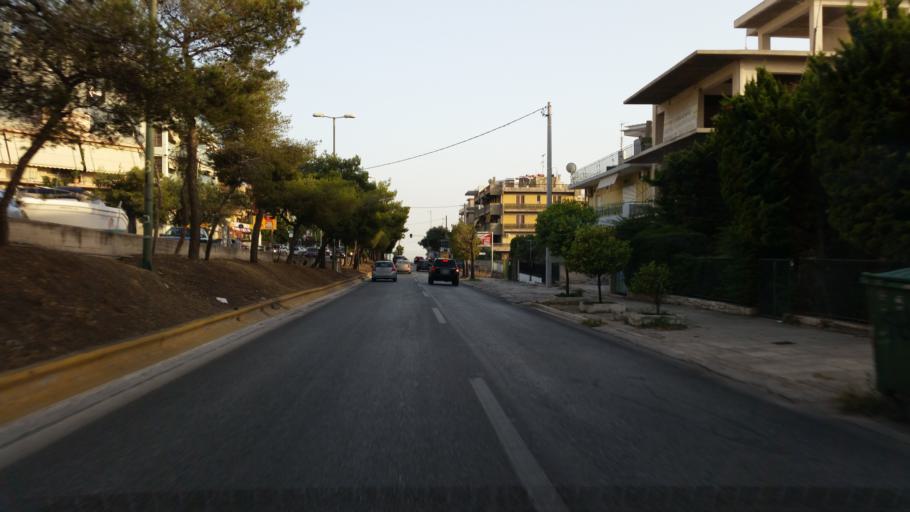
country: GR
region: Attica
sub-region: Nomarchia Athinas
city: Ilioupoli
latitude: 37.9216
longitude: 23.7553
